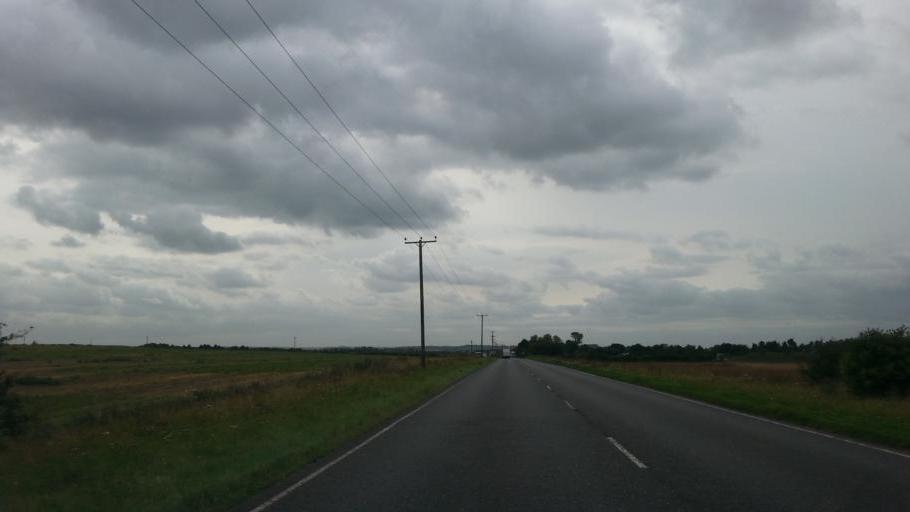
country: GB
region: England
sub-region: Cambridgeshire
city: Harston
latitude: 52.0753
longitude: 0.0821
